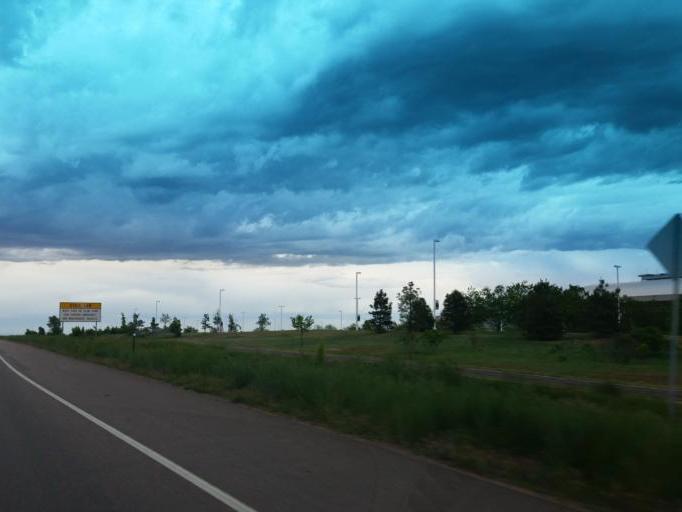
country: US
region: Colorado
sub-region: Larimer County
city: Loveland
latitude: 40.4427
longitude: -104.9919
